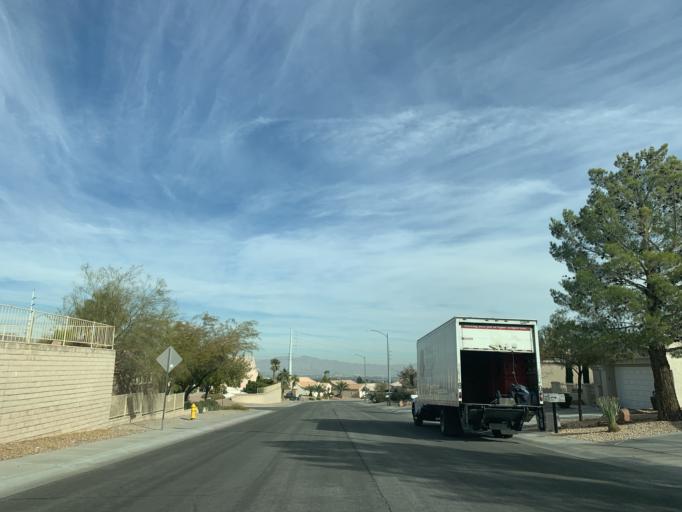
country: US
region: Nevada
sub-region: Clark County
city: Summerlin South
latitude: 36.2170
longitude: -115.3266
